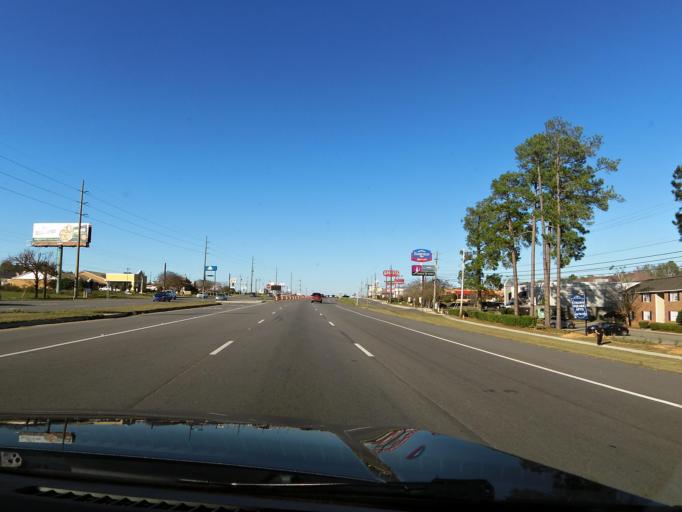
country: US
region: Alabama
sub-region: Houston County
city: Dothan
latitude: 31.2224
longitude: -85.4323
